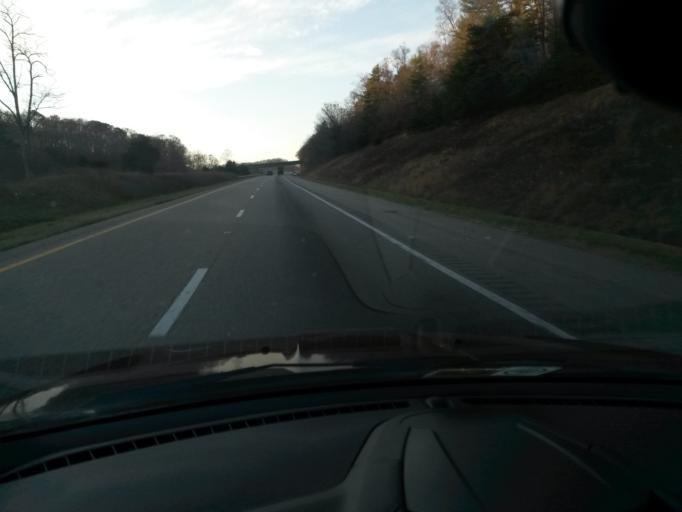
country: US
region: Virginia
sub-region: City of Lexington
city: Lexington
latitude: 37.8803
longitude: -79.5439
